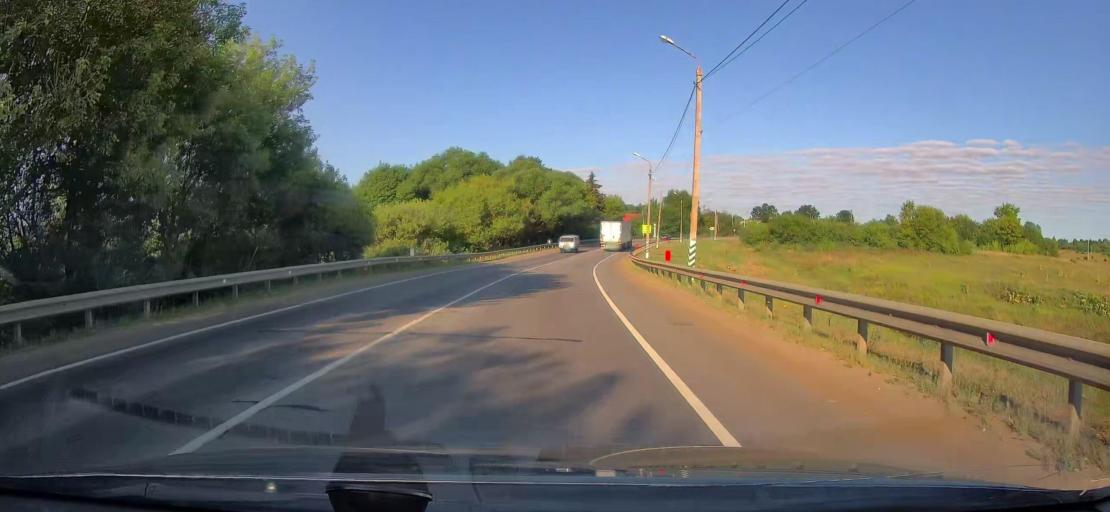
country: RU
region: Tula
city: Chern'
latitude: 53.4513
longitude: 36.8910
